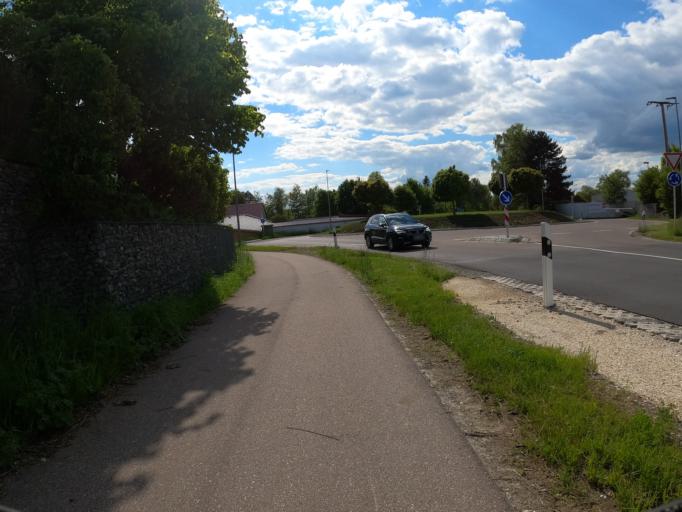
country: DE
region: Bavaria
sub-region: Swabia
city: Wasserburg
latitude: 48.4363
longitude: 10.2605
